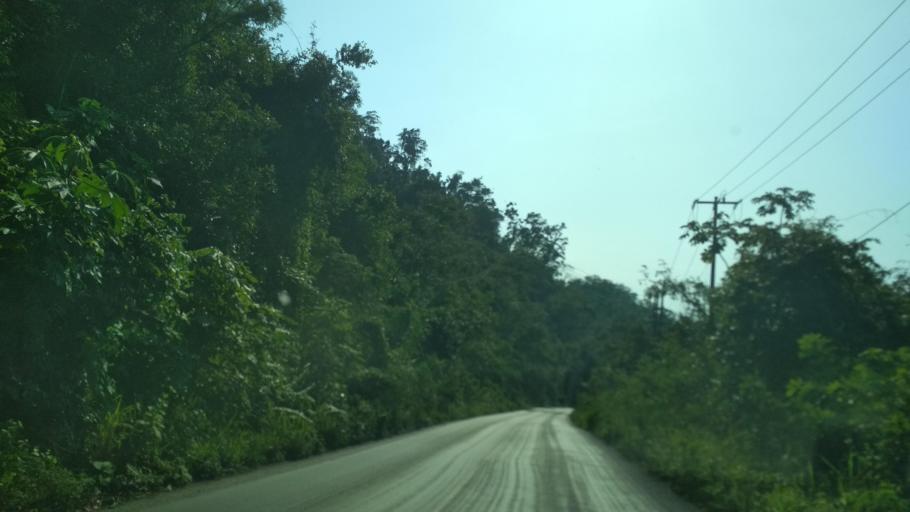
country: MX
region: Veracruz
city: Agua Dulce
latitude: 20.3954
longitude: -97.2340
